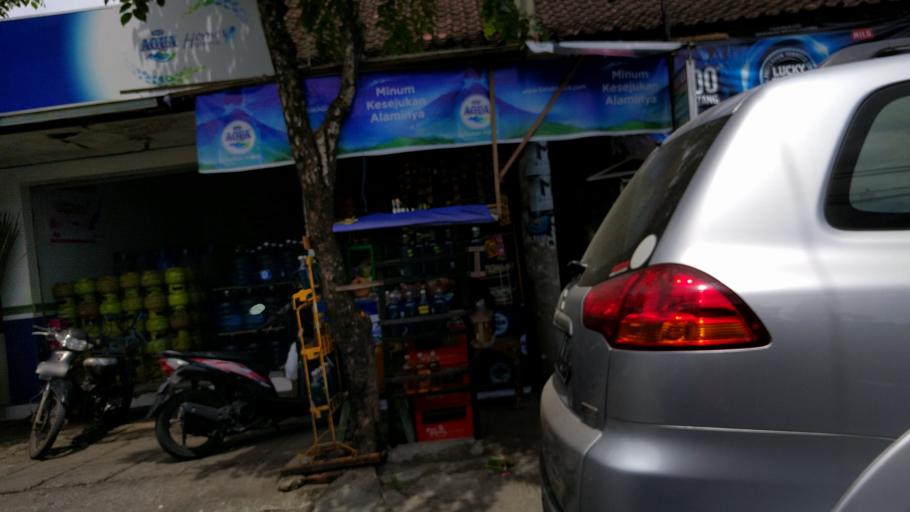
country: ID
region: Bali
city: Banjar Gunungpande
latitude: -8.6580
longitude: 115.1471
